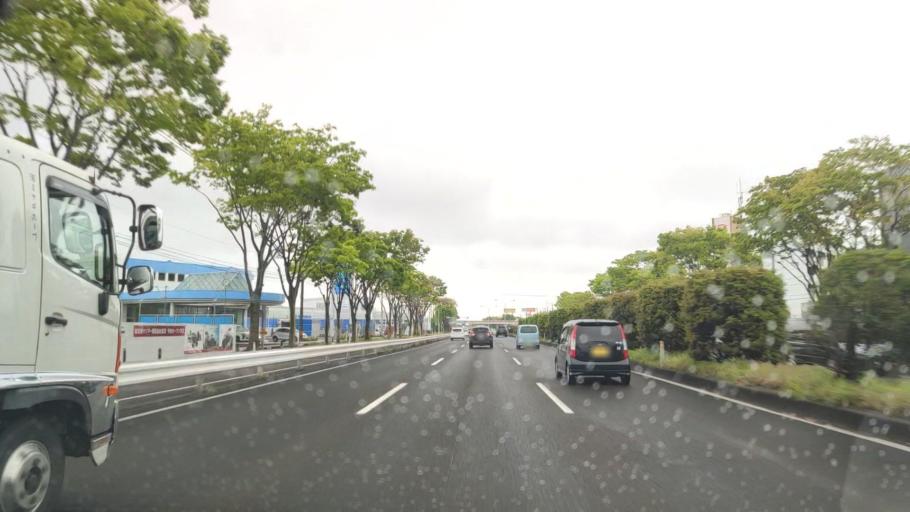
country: JP
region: Miyagi
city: Sendai
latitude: 38.2346
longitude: 140.9108
